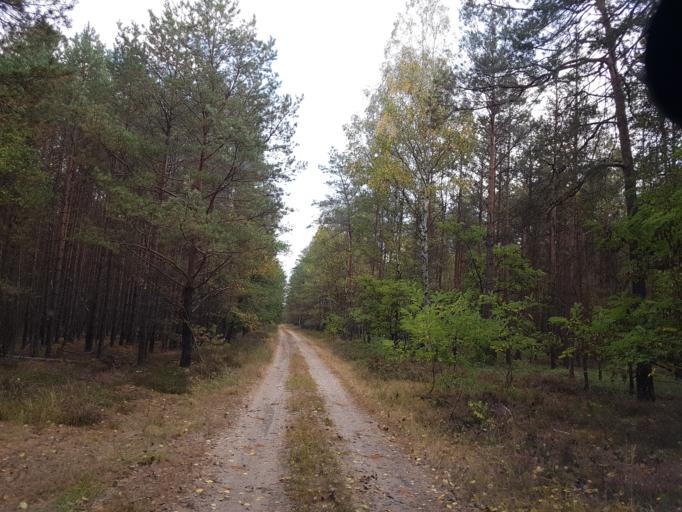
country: DE
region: Brandenburg
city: Finsterwalde
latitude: 51.5928
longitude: 13.7431
